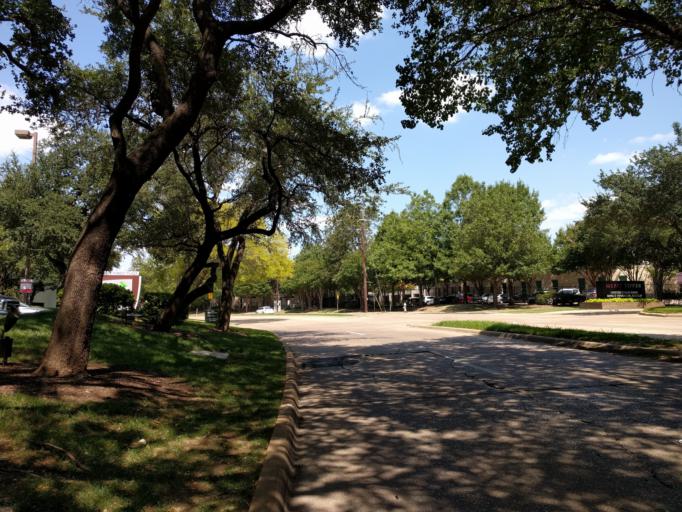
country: US
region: Texas
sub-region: Dallas County
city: Richardson
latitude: 32.9145
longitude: -96.7720
